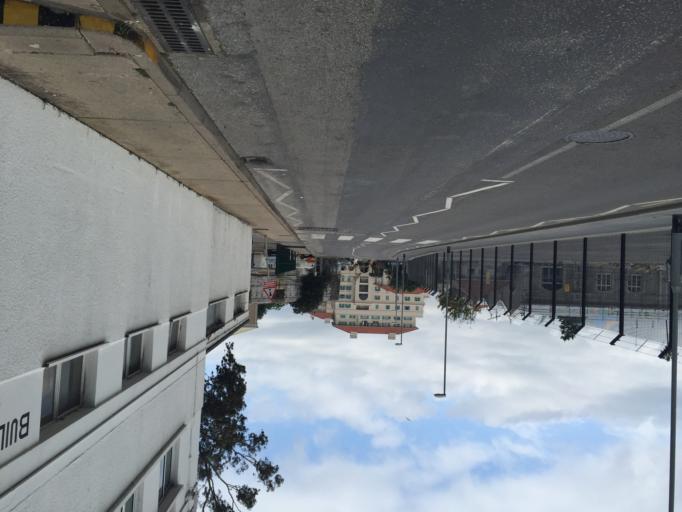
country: GI
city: Gibraltar
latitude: 36.1327
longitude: -5.3533
